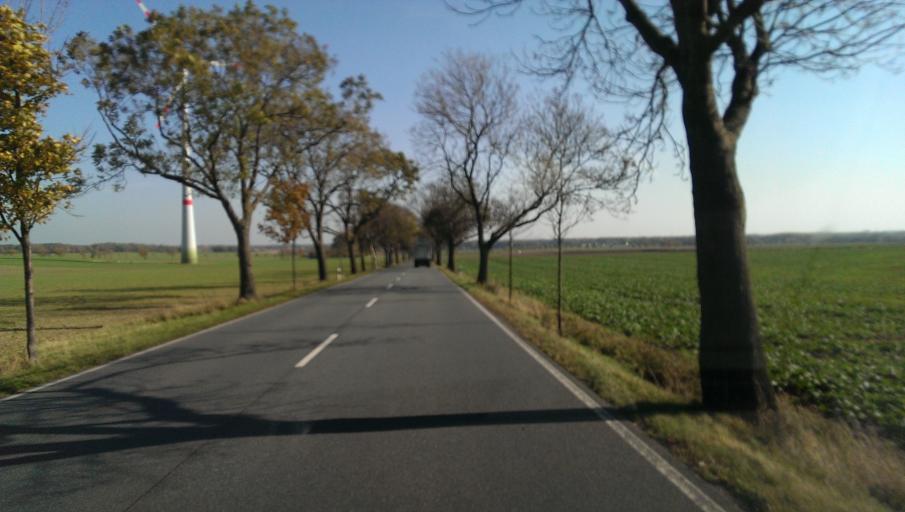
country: DE
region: Saxony
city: Stauchitz
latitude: 51.2749
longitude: 13.2115
